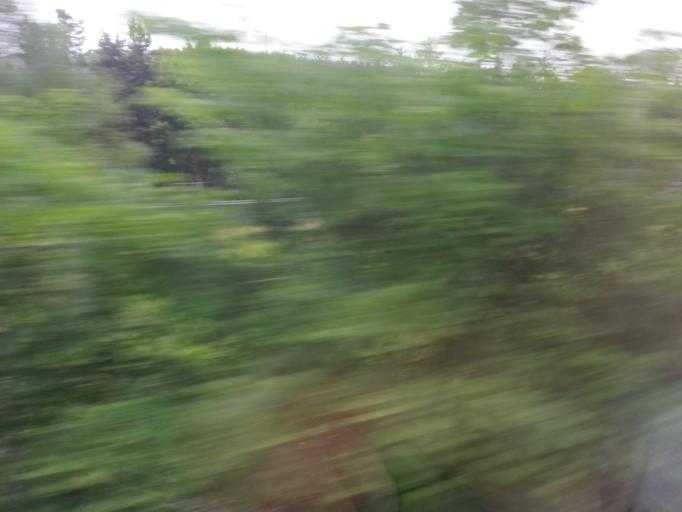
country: GB
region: Scotland
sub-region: Perth and Kinross
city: Bankfoot
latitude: 56.5529
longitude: -3.5667
